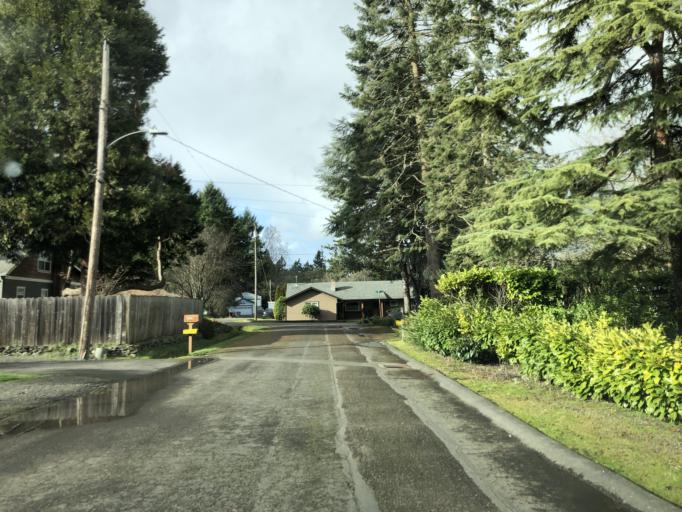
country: US
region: Oregon
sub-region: Washington County
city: Tigard
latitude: 45.4231
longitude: -122.7869
